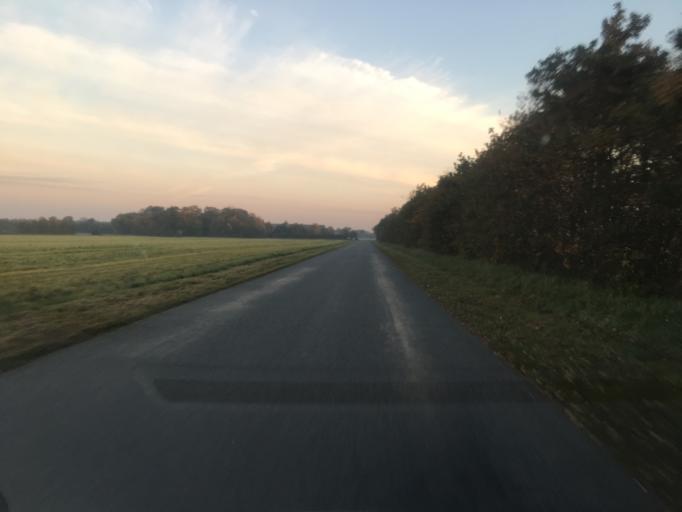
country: DK
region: South Denmark
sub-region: Tonder Kommune
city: Logumkloster
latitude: 55.0128
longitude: 9.0480
